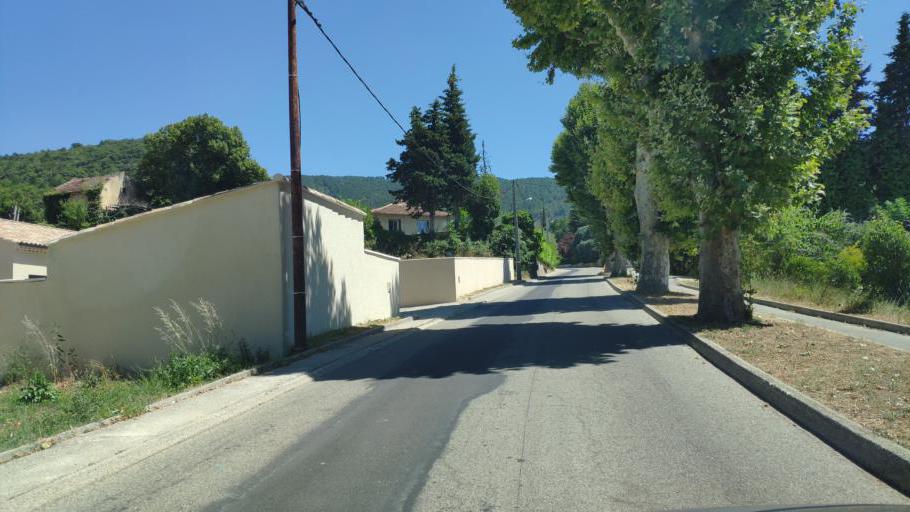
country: FR
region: Provence-Alpes-Cote d'Azur
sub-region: Departement du Vaucluse
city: Malaucene
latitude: 44.1728
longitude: 5.1370
